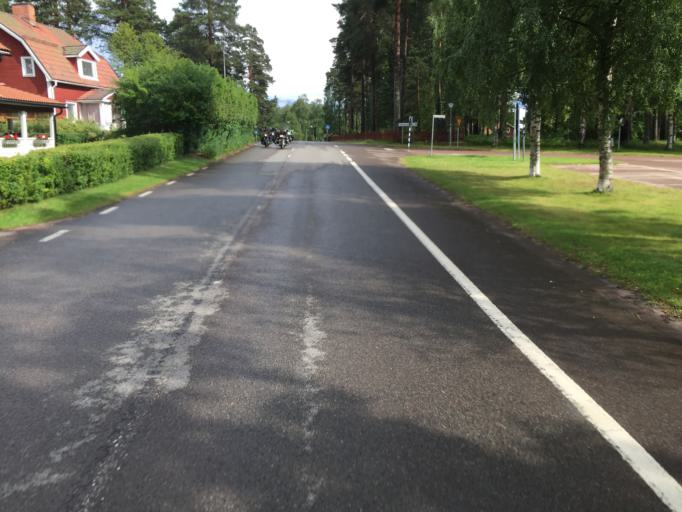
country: SE
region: Dalarna
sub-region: Vansbro Kommun
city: Vansbro
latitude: 60.5166
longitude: 14.2317
